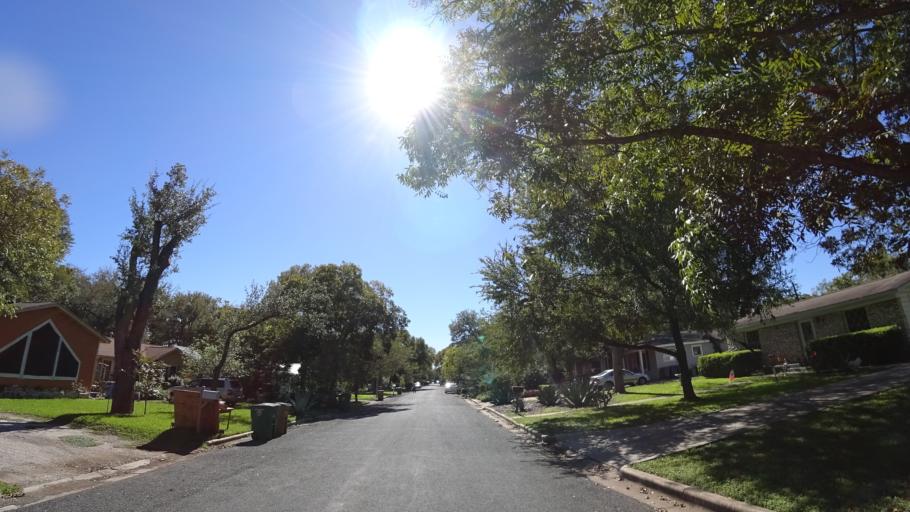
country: US
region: Texas
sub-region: Travis County
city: Rollingwood
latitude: 30.2220
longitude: -97.7801
